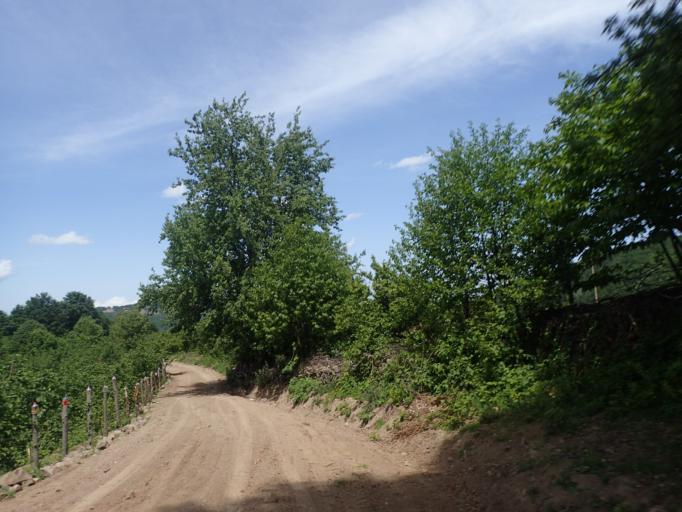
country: TR
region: Ordu
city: Caybasi
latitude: 40.9011
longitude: 37.0753
